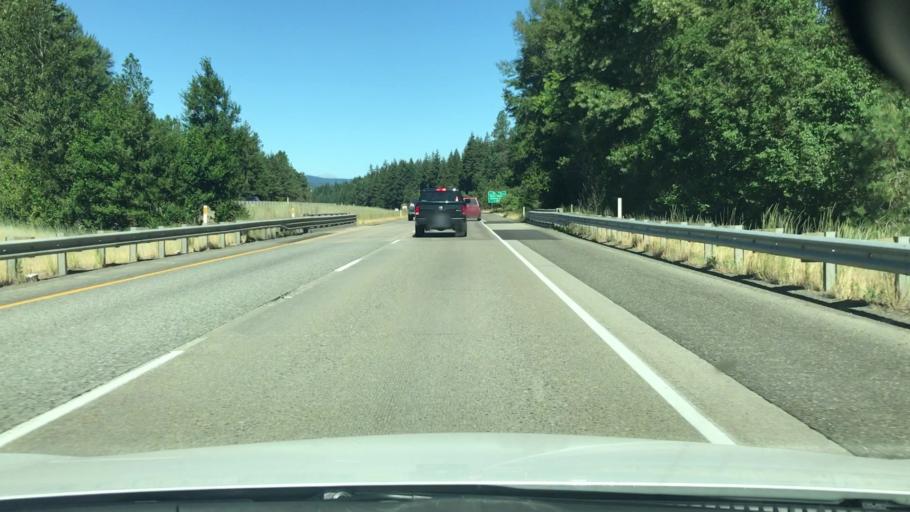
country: US
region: Washington
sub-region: Kittitas County
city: Cle Elum
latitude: 47.2122
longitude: -121.1030
